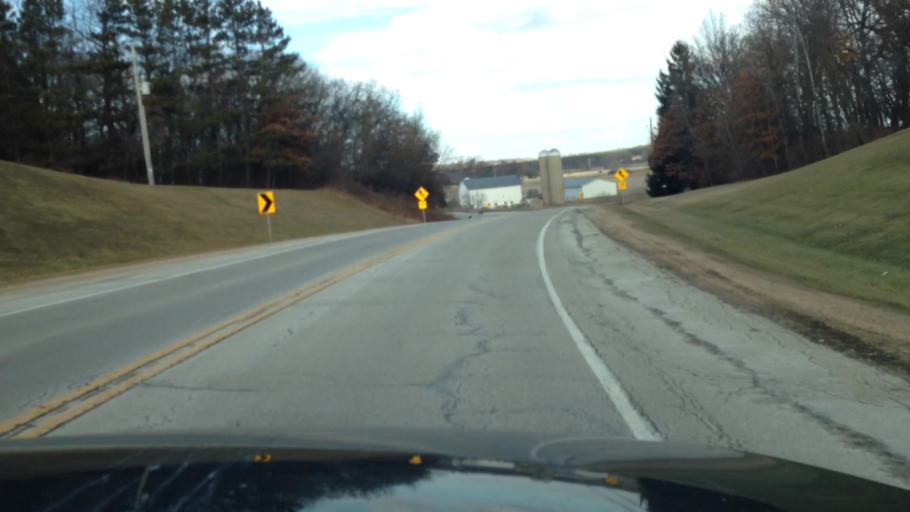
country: US
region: Wisconsin
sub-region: Walworth County
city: Lake Geneva
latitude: 42.6319
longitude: -88.4135
